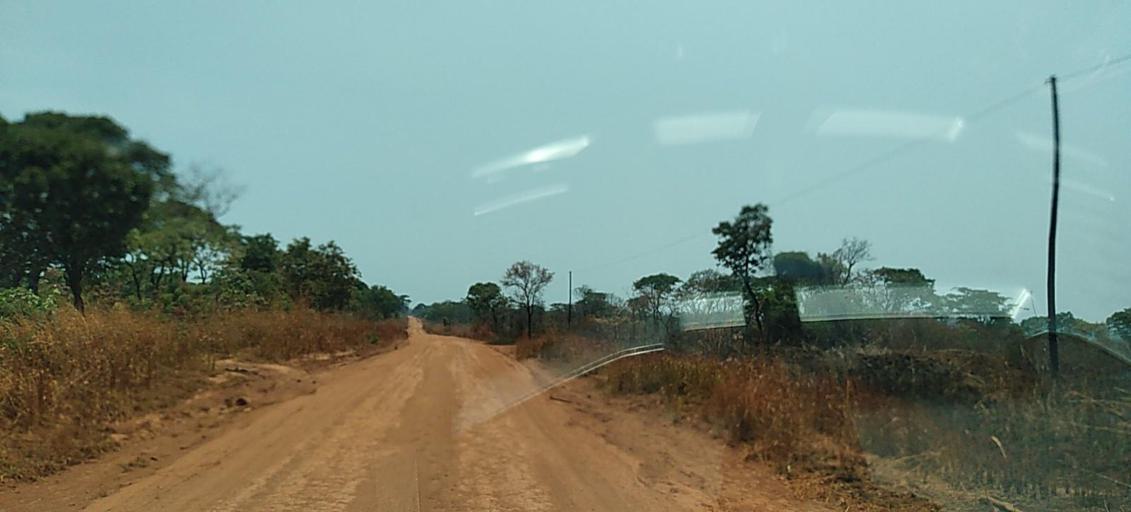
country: CD
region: Katanga
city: Kipushi
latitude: -11.9701
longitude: 26.8987
